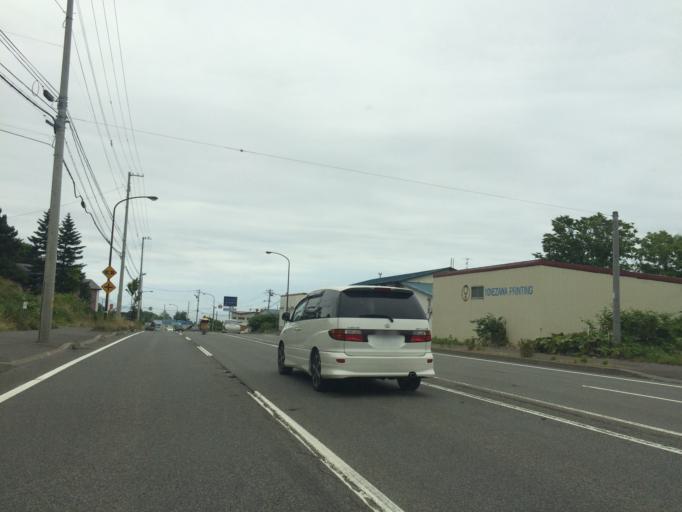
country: JP
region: Hokkaido
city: Otaru
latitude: 43.1474
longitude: 141.1374
